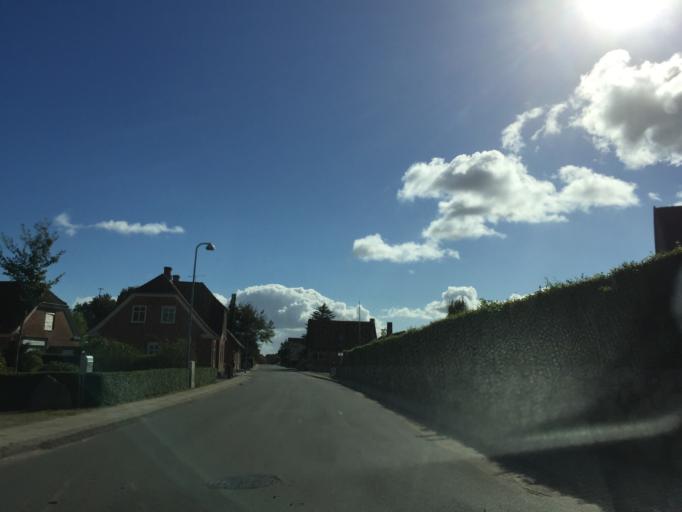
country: DK
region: Central Jutland
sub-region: Viborg Kommune
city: Bjerringbro
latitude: 56.4110
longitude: 9.6131
